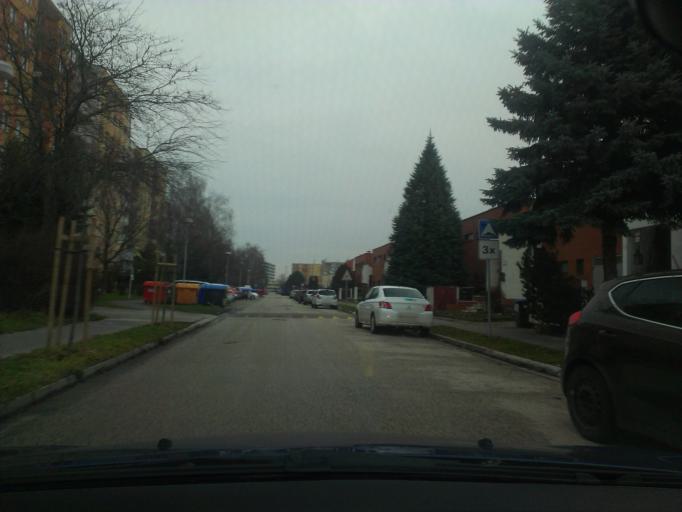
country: SK
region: Trnavsky
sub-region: Okres Trnava
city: Piestany
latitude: 48.5825
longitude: 17.8202
